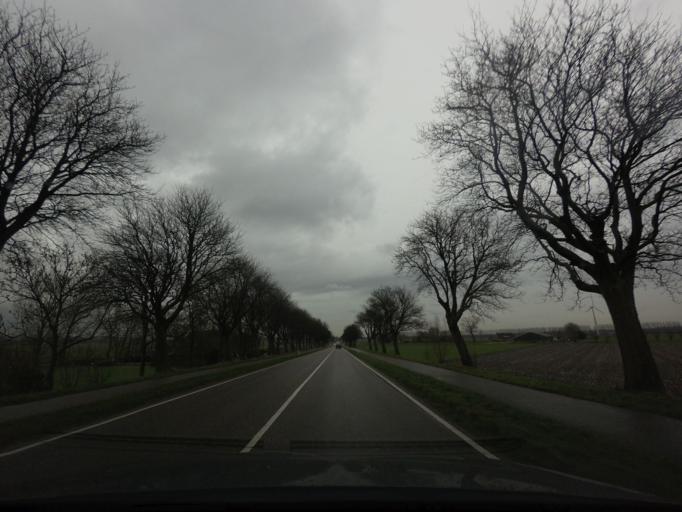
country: NL
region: North Brabant
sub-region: Gemeente Moerdijk
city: Klundert
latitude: 51.6240
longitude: 4.6352
